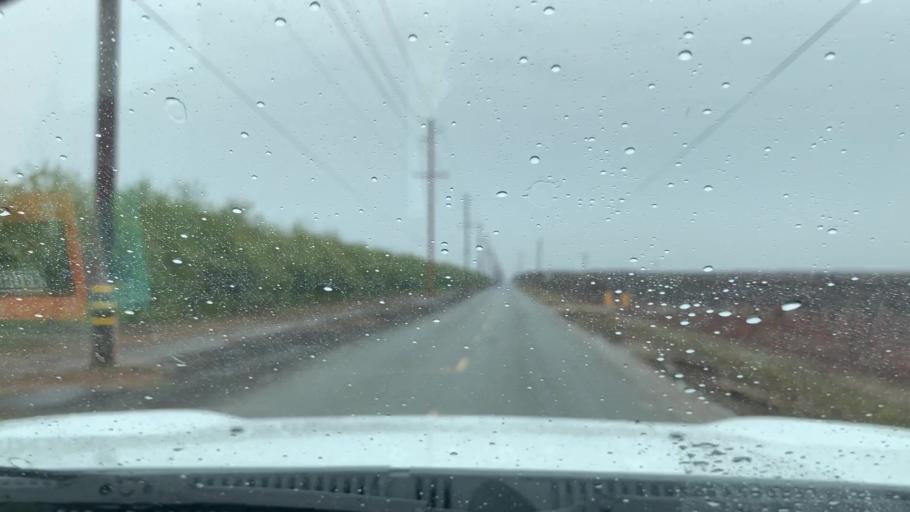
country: US
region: California
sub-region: Kern County
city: Delano
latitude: 35.8340
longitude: -119.1951
